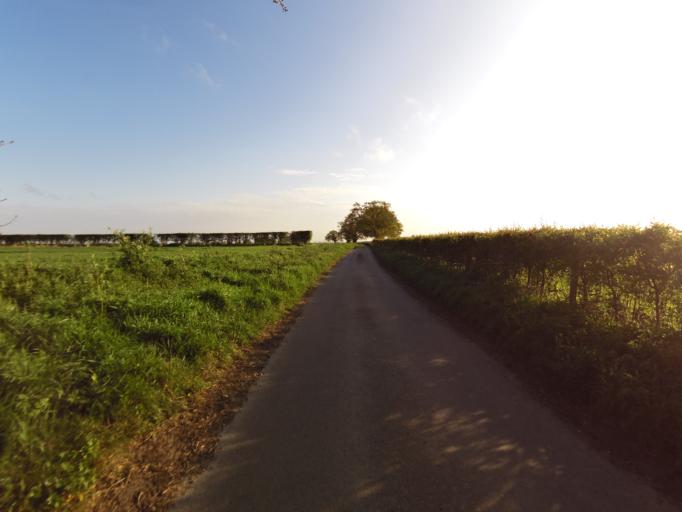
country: GB
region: England
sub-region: Suffolk
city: Capel Saint Mary
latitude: 52.0349
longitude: 1.0700
